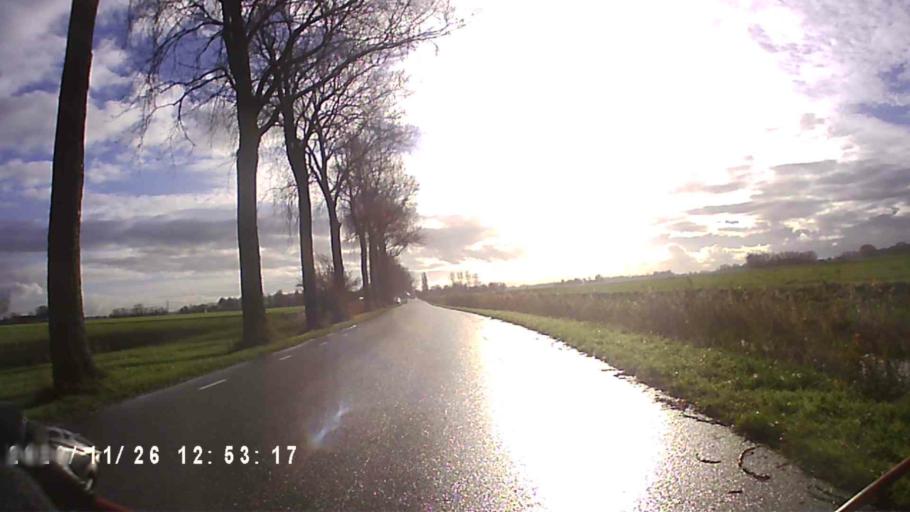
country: NL
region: Groningen
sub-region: Gemeente Appingedam
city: Appingedam
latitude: 53.3519
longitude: 6.7908
